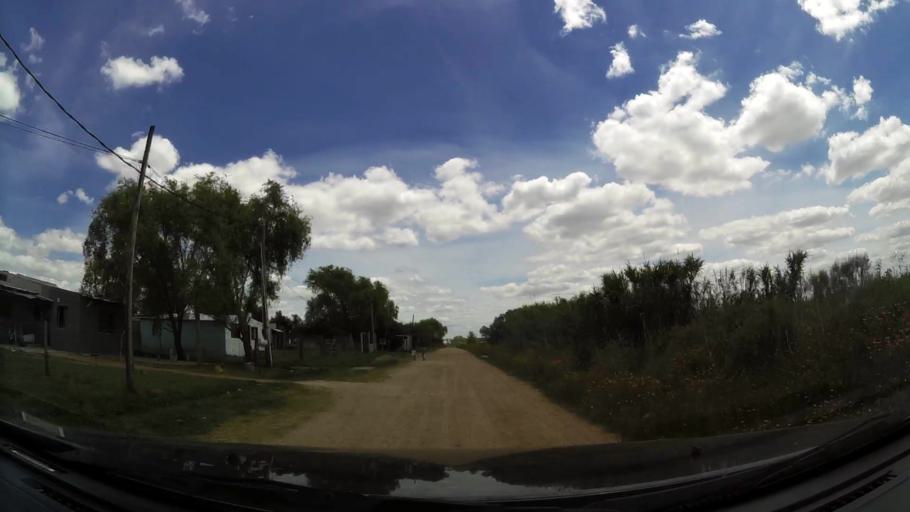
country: UY
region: Canelones
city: Colonia Nicolich
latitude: -34.8165
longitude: -55.9996
